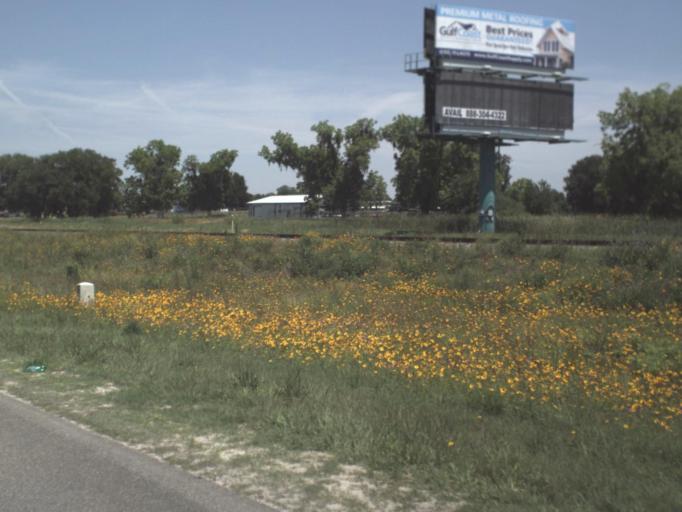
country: US
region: Florida
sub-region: Suwannee County
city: Live Oak
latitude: 30.2852
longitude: -82.9575
